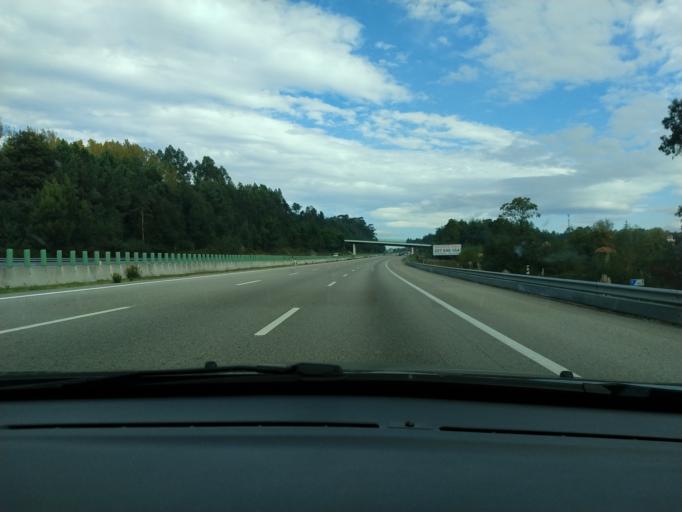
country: PT
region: Aveiro
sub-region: Santa Maria da Feira
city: Feira
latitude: 40.8952
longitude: -8.5683
